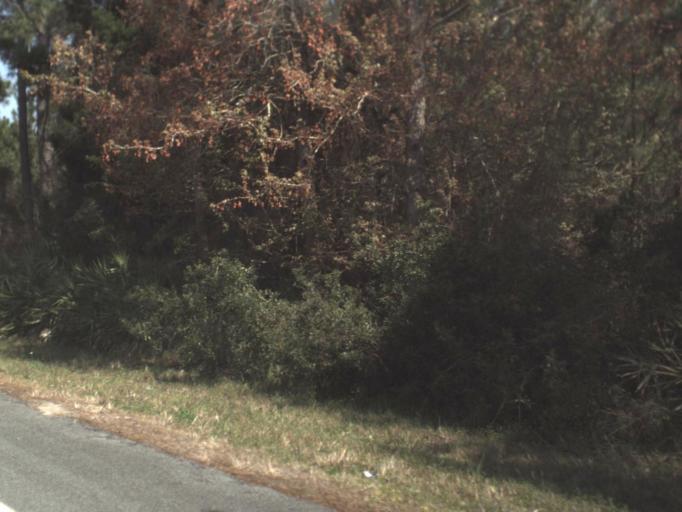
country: US
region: Florida
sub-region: Franklin County
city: Carrabelle
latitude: 29.9319
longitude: -84.5111
